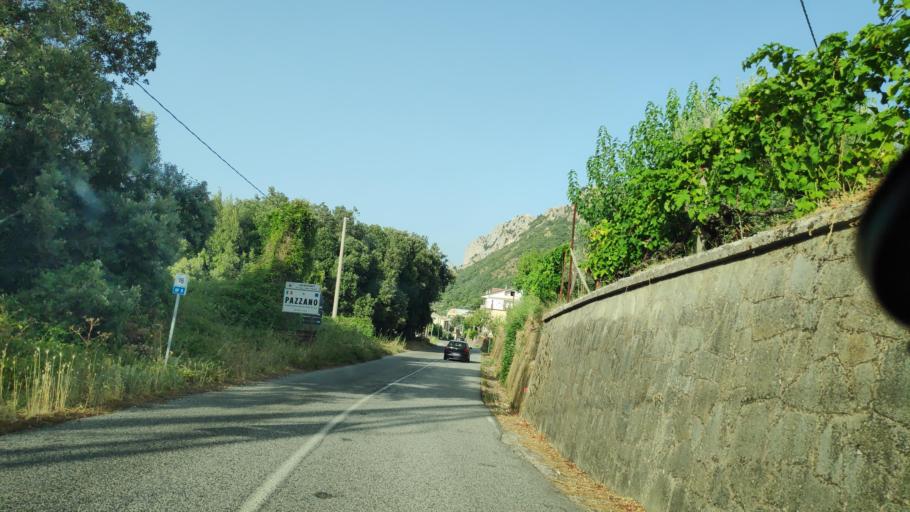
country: IT
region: Calabria
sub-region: Provincia di Reggio Calabria
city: Pazzano
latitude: 38.4781
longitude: 16.4482
